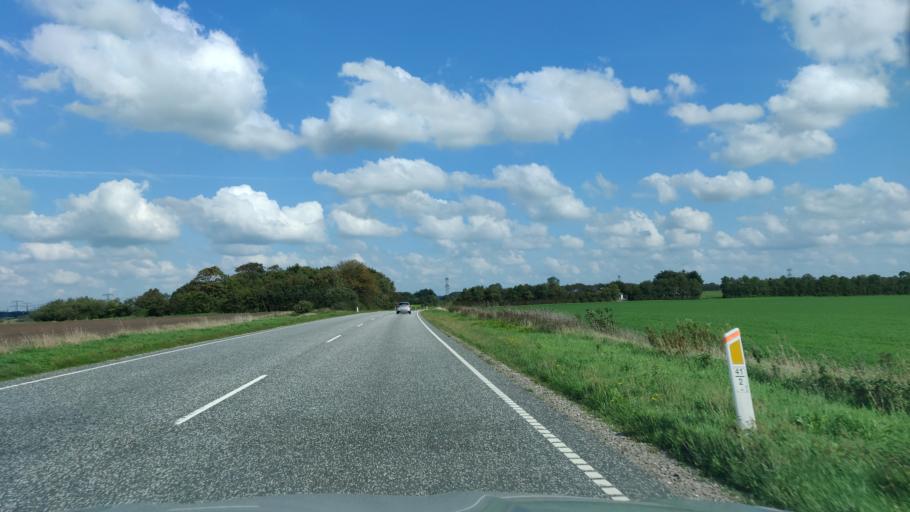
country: DK
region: North Denmark
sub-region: Vesthimmerland Kommune
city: Aars
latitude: 56.7892
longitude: 9.6025
